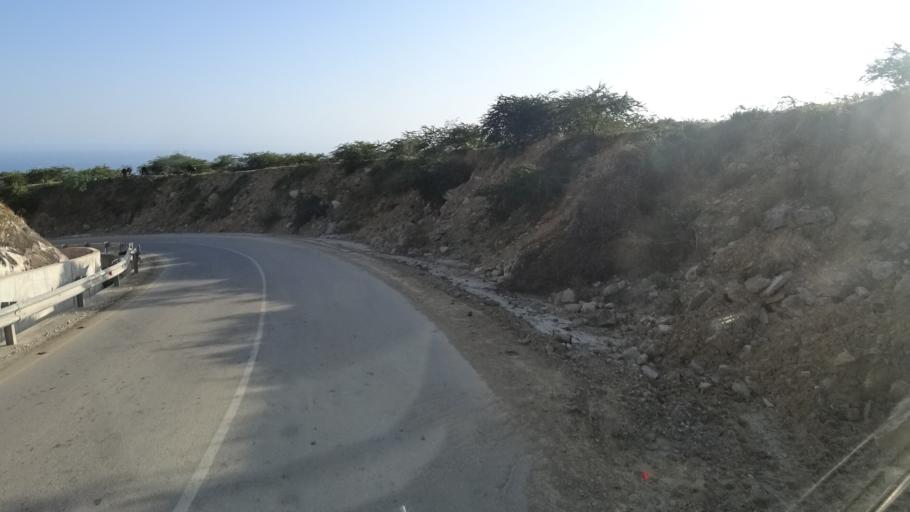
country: OM
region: Zufar
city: Salalah
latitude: 17.0557
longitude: 54.6110
